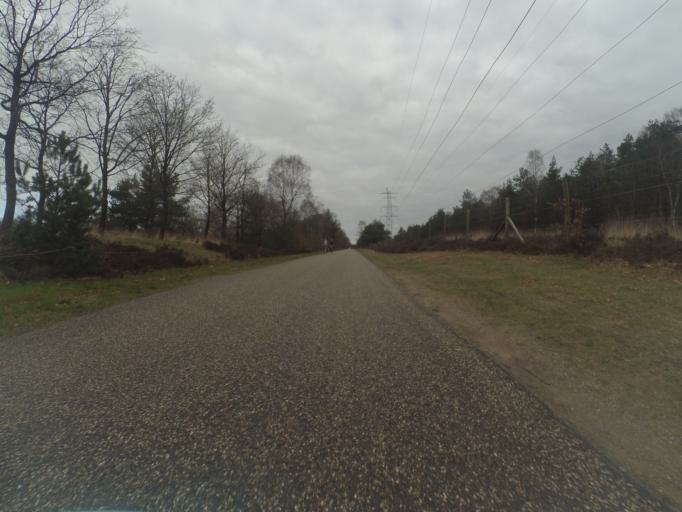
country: NL
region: Gelderland
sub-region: Gemeente Rozendaal
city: Rozendaal
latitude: 52.0416
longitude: 5.9342
